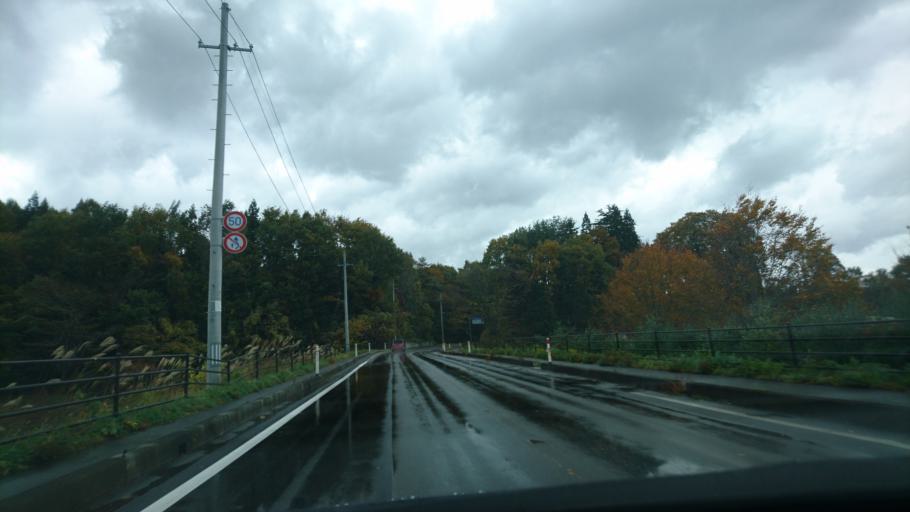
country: JP
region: Iwate
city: Shizukuishi
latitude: 39.6662
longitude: 140.9695
